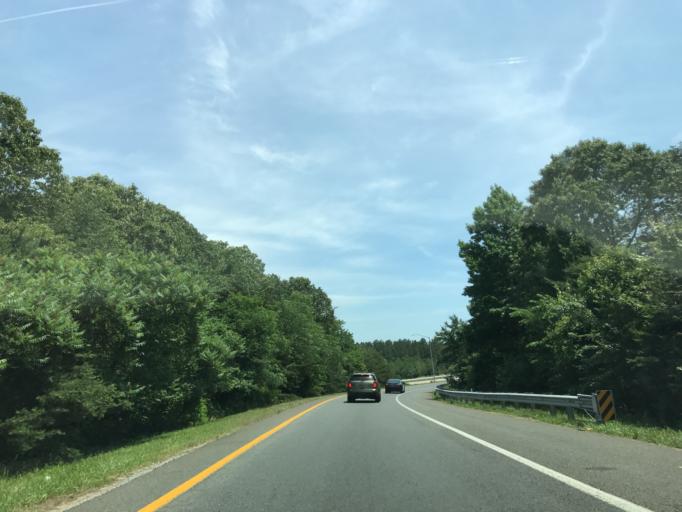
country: US
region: Maryland
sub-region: Anne Arundel County
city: Glen Burnie
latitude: 39.1508
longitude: -76.6467
